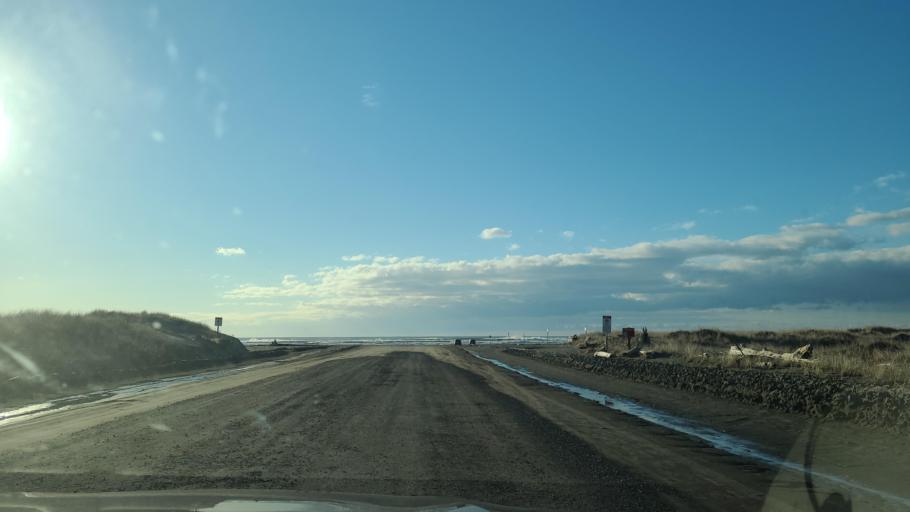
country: US
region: Washington
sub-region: Grays Harbor County
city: Ocean Shores
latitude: 46.9940
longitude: -124.1716
